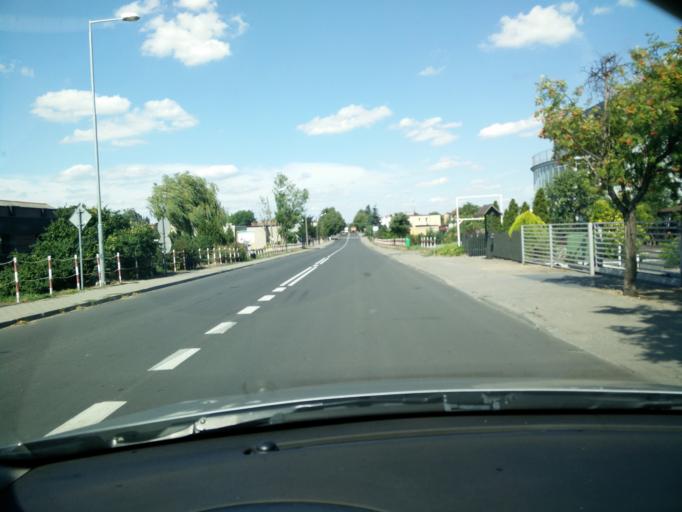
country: PL
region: Greater Poland Voivodeship
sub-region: Powiat sredzki
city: Sroda Wielkopolska
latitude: 52.2268
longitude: 17.2889
